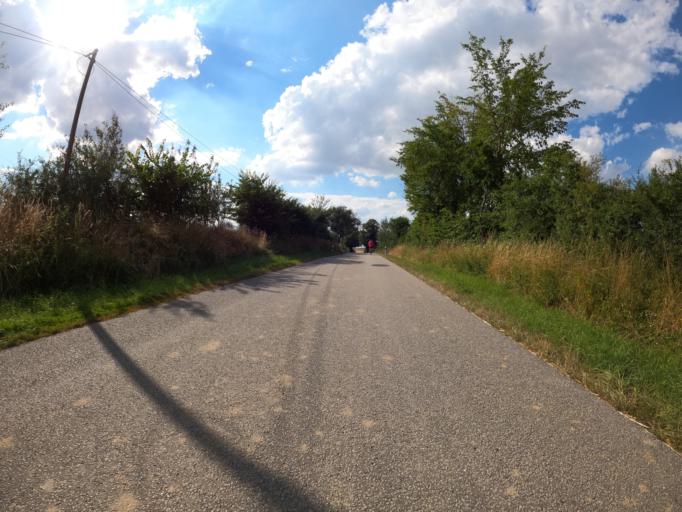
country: DE
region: Mecklenburg-Vorpommern
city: Woldegk
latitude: 53.4448
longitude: 13.5873
